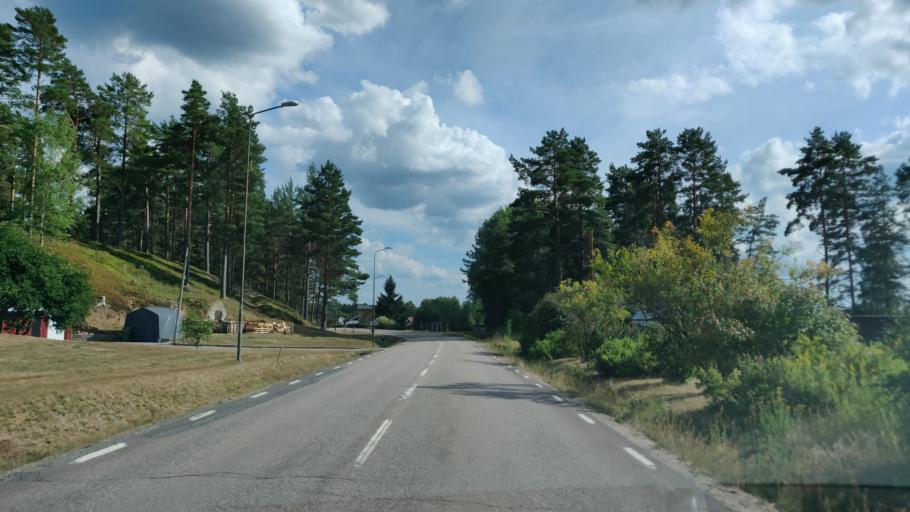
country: SE
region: Vaermland
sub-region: Hagfors Kommun
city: Ekshaerad
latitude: 60.1153
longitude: 13.5633
